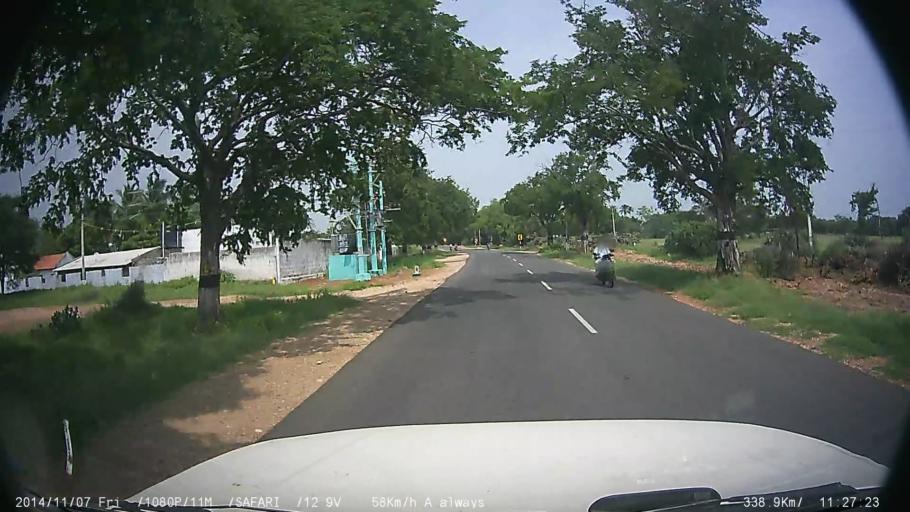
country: IN
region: Tamil Nadu
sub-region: Tiruppur
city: Avinashi
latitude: 11.1368
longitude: 77.2665
